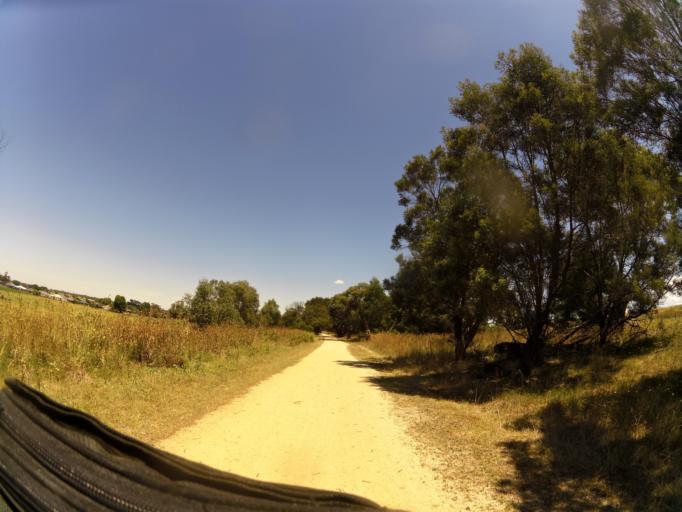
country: AU
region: Victoria
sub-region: Wellington
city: Sale
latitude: -37.9728
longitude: 146.9919
